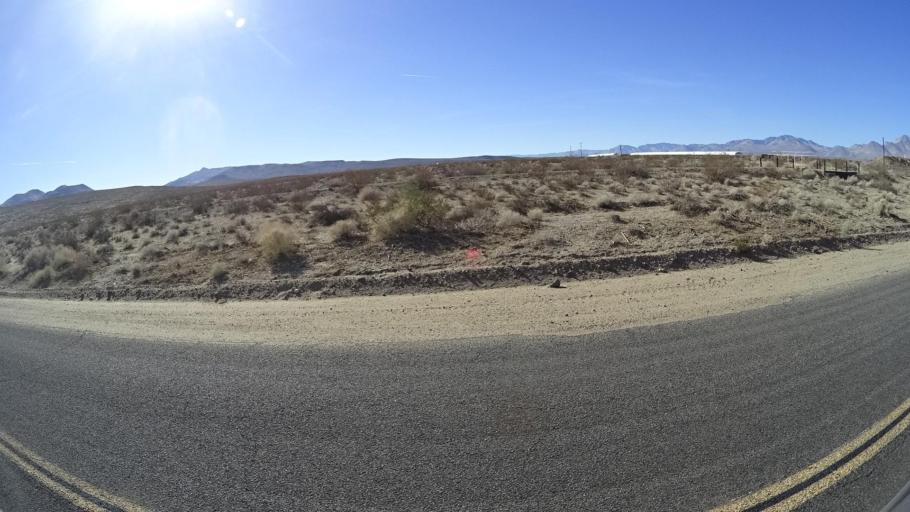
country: US
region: California
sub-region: Kern County
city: China Lake Acres
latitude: 35.5665
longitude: -117.7761
